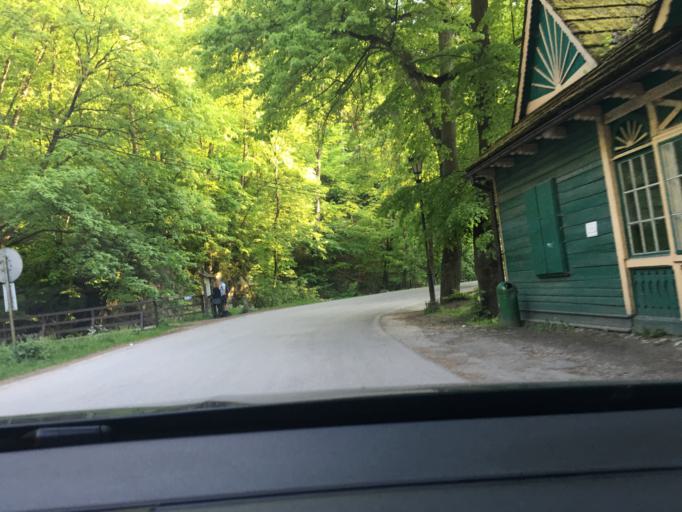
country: PL
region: Lesser Poland Voivodeship
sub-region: Powiat krakowski
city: Skala
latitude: 50.2113
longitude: 19.8319
